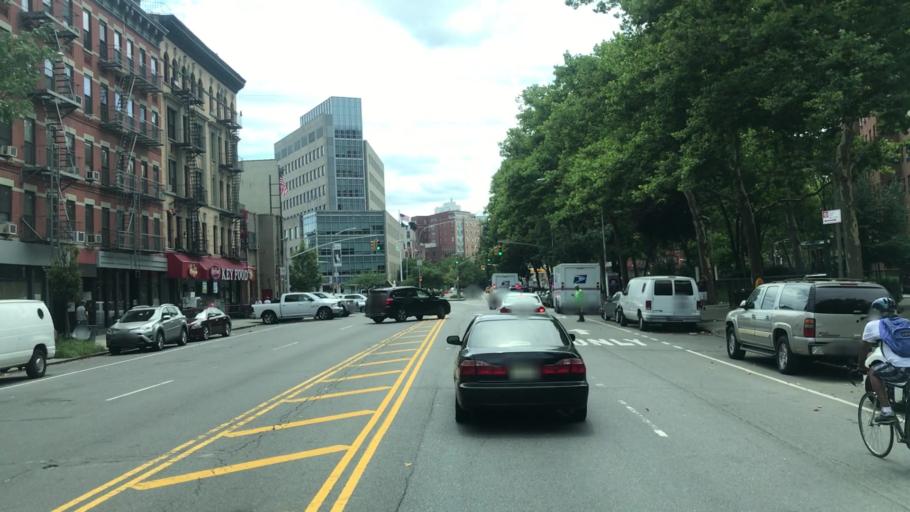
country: US
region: New Jersey
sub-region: Bergen County
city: Edgewater
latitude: 40.8124
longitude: -73.9554
